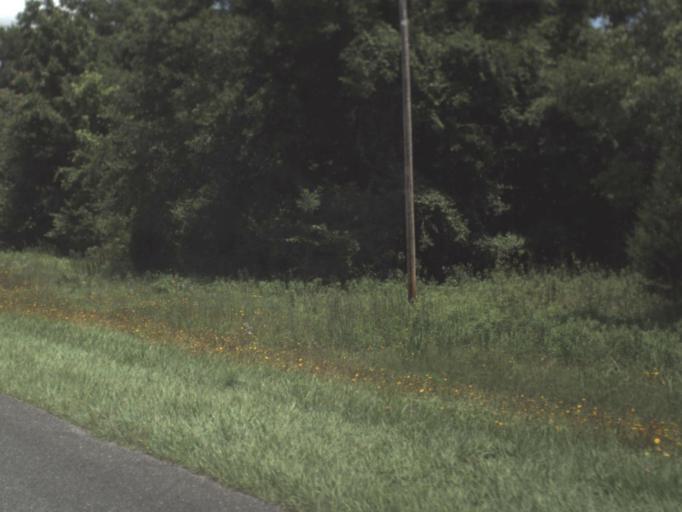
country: US
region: Florida
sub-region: Alachua County
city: High Springs
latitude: 29.8803
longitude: -82.6631
